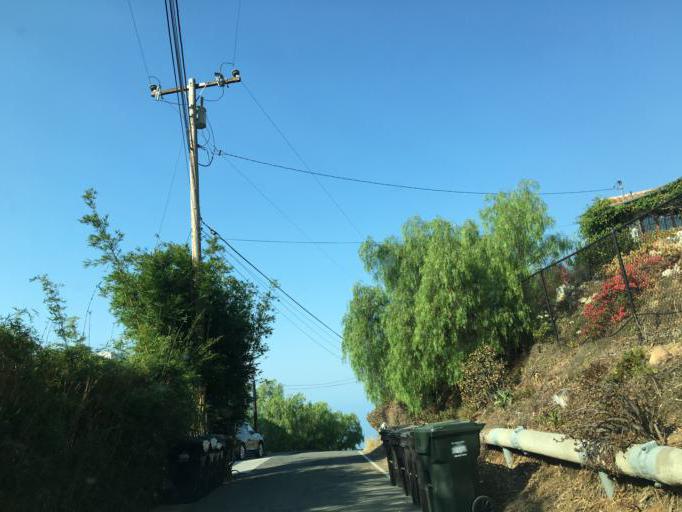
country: US
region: California
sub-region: Los Angeles County
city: Las Flores
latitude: 34.0522
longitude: -118.6444
